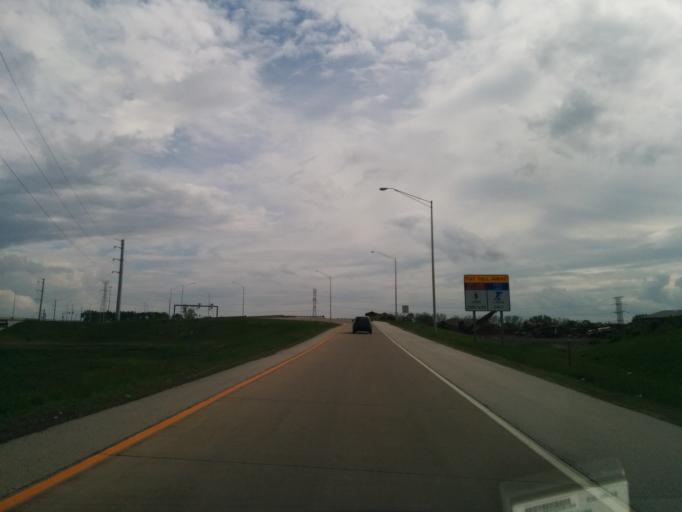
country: US
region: Illinois
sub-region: Cook County
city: Lemont
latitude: 41.6380
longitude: -88.0129
